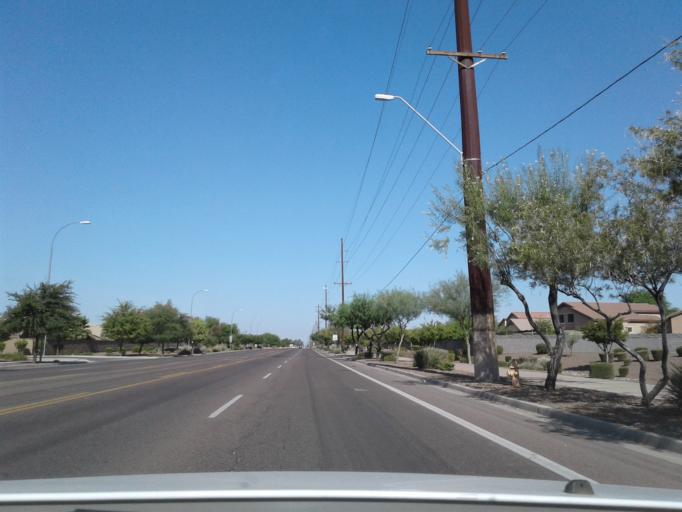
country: US
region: Arizona
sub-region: Maricopa County
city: Laveen
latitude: 33.3920
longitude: -112.1736
